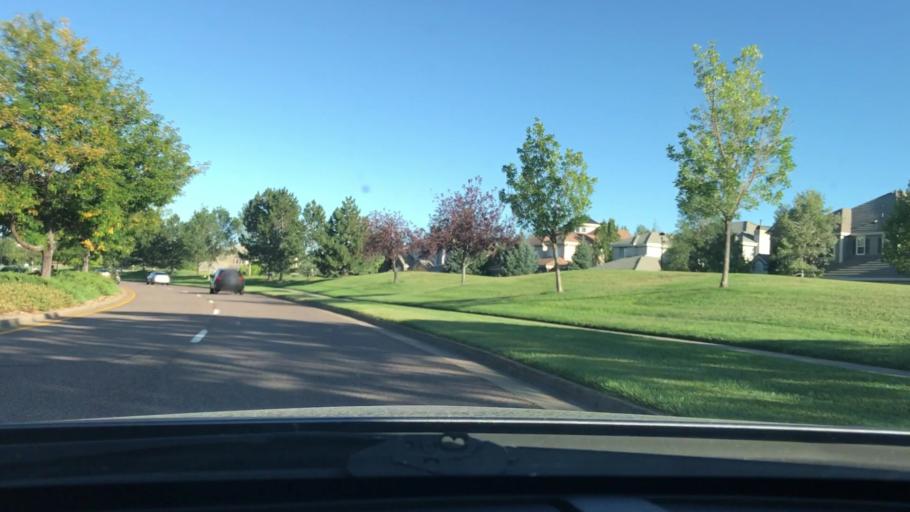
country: US
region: Colorado
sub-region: Arapahoe County
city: Dove Valley
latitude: 39.6071
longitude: -104.7667
